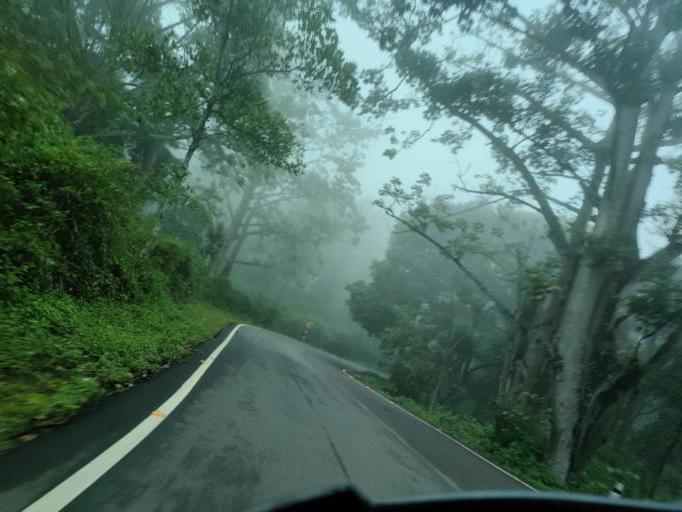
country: IN
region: Tamil Nadu
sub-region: Dindigul
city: Ayakudi
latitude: 10.3552
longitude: 77.5680
